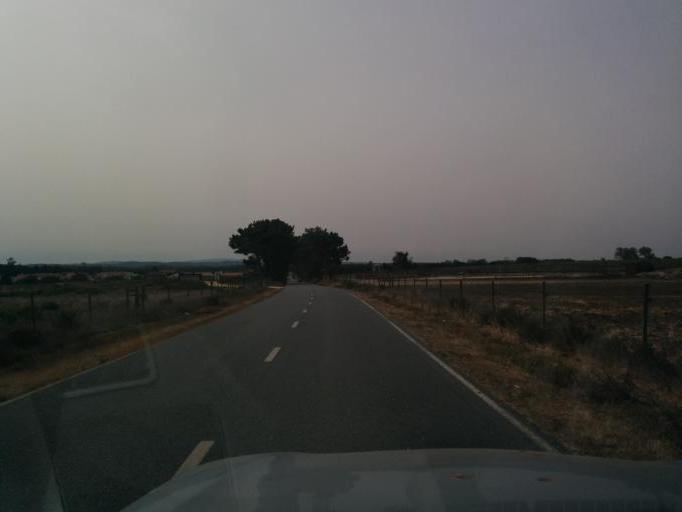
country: PT
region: Beja
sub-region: Odemira
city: Sao Teotonio
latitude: 37.5953
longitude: -8.7428
